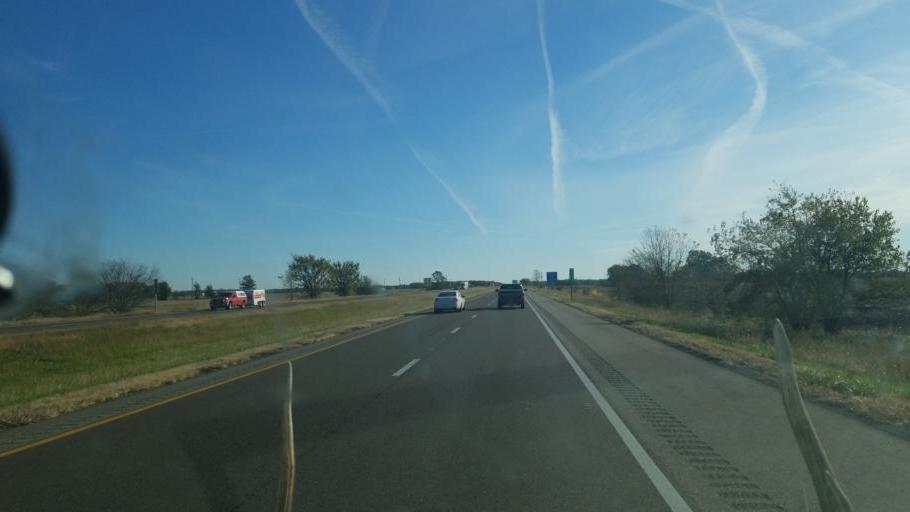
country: US
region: Illinois
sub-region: Madison County
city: Highland
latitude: 38.7844
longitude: -89.7278
